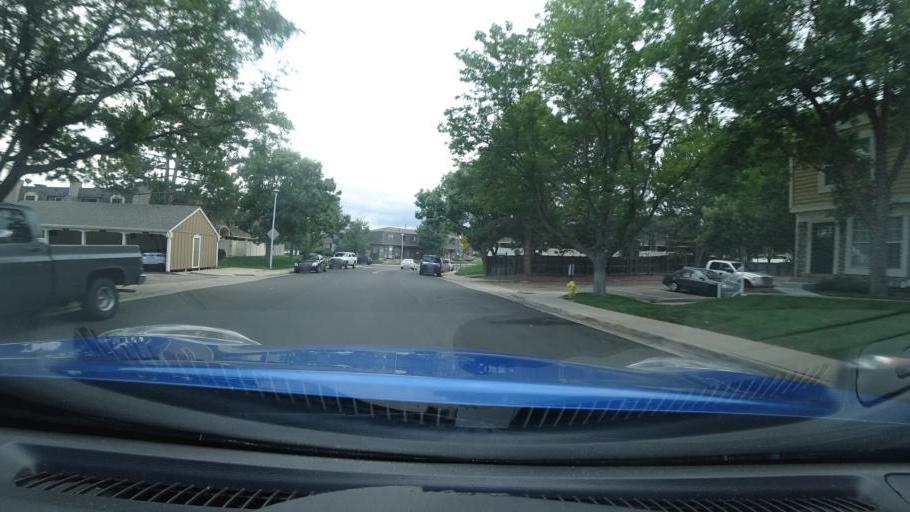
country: US
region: Colorado
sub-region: Adams County
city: Aurora
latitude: 39.6926
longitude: -104.8065
